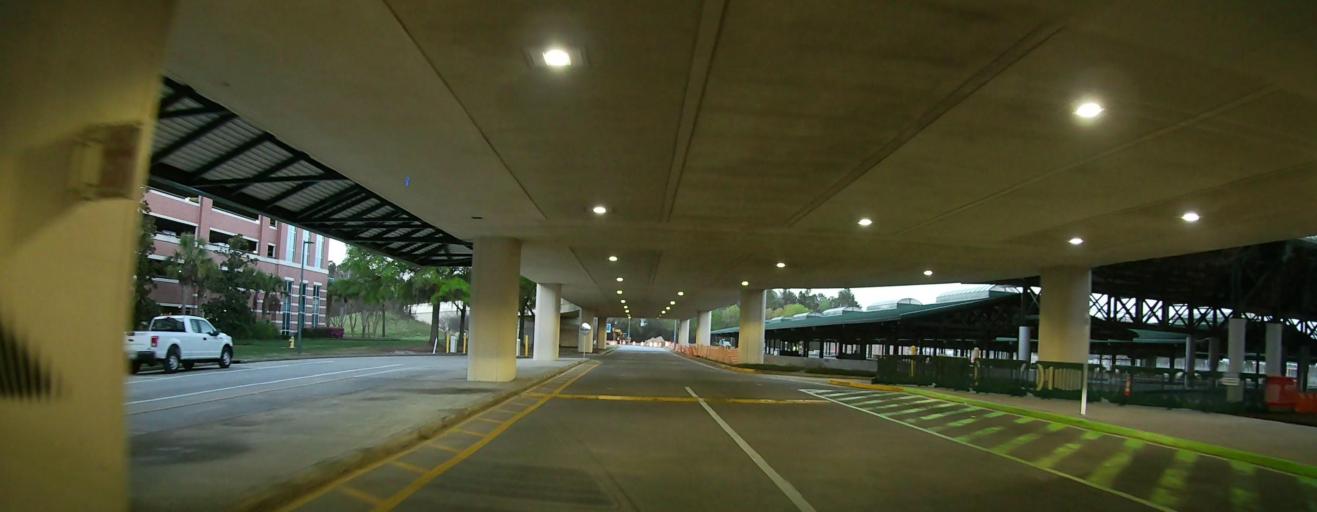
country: US
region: Georgia
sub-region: Chatham County
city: Pooler
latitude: 32.1367
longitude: -81.2103
